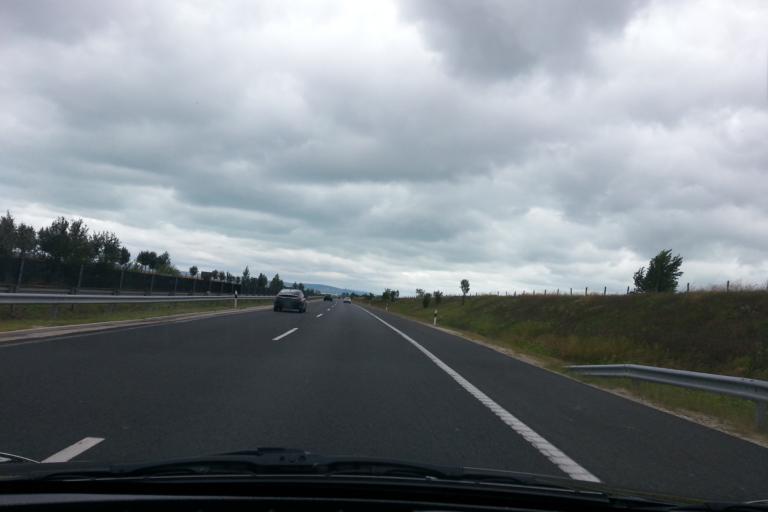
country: HU
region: Somogy
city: Zamardi
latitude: 46.8634
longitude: 17.9664
